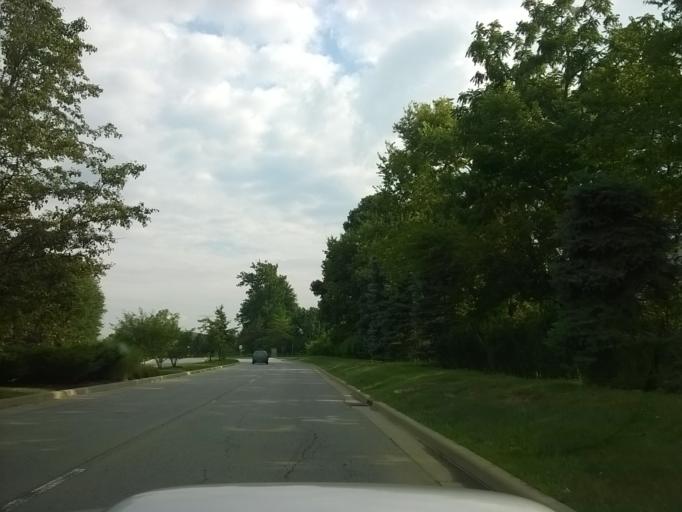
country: US
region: Indiana
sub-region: Hamilton County
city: Carmel
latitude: 39.9751
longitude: -86.1625
